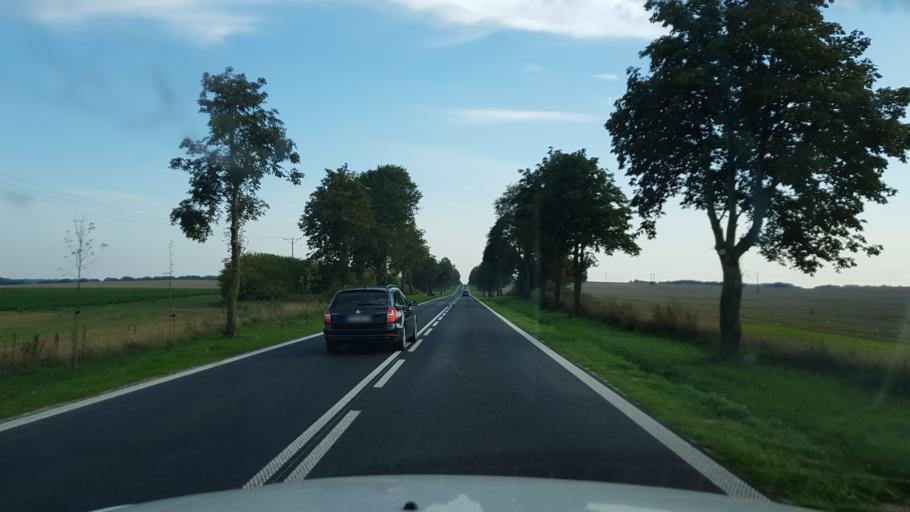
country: PL
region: West Pomeranian Voivodeship
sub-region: Powiat gryficki
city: Ploty
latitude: 53.8378
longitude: 15.2390
